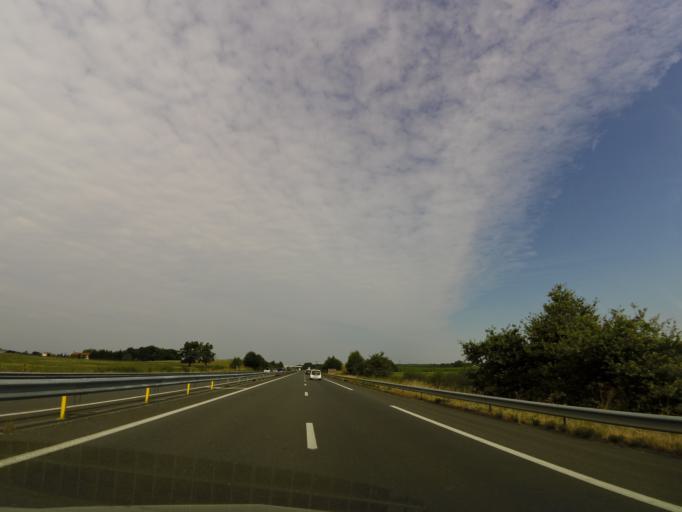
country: FR
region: Pays de la Loire
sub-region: Departement de la Loire-Atlantique
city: Le Bignon
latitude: 47.0951
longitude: -1.4658
